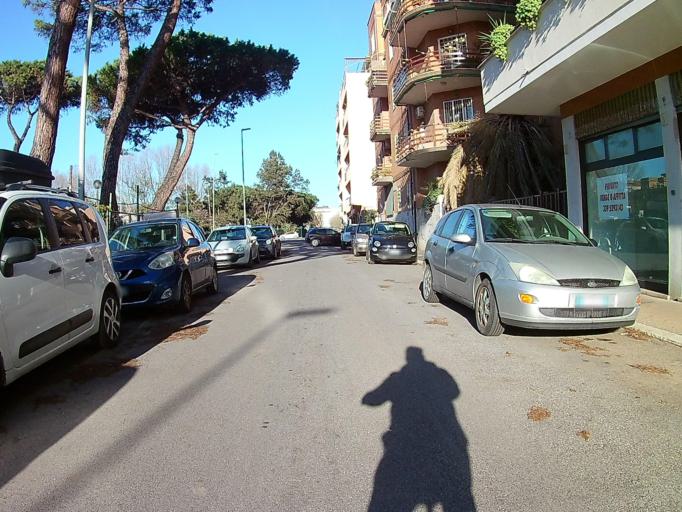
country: IT
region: Latium
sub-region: Citta metropolitana di Roma Capitale
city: Lido di Ostia
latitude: 41.7328
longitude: 12.2868
